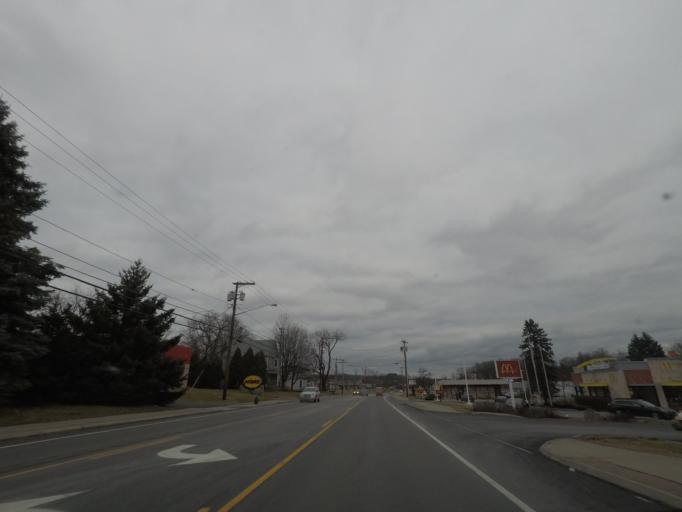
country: US
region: New York
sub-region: Rensselaer County
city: Wynantskill
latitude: 42.7478
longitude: -73.6385
